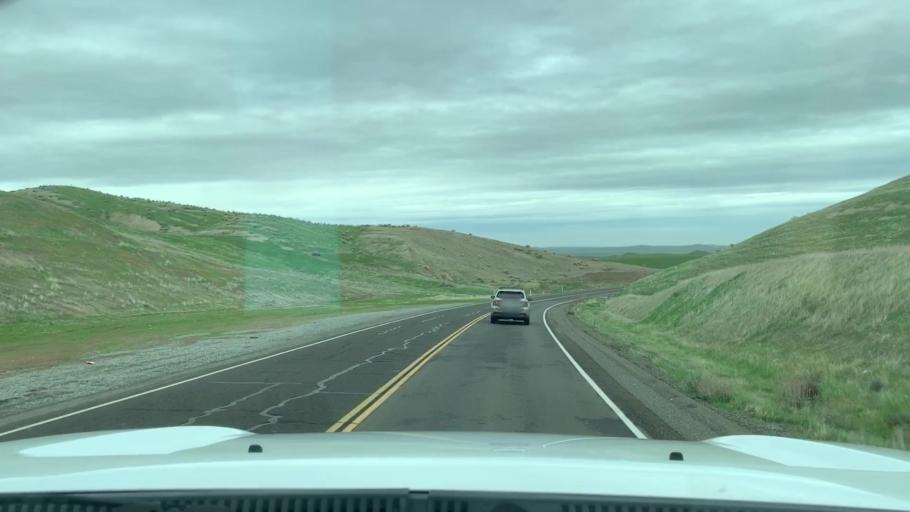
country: US
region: California
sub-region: Kings County
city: Avenal
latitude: 35.8607
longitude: -120.0806
